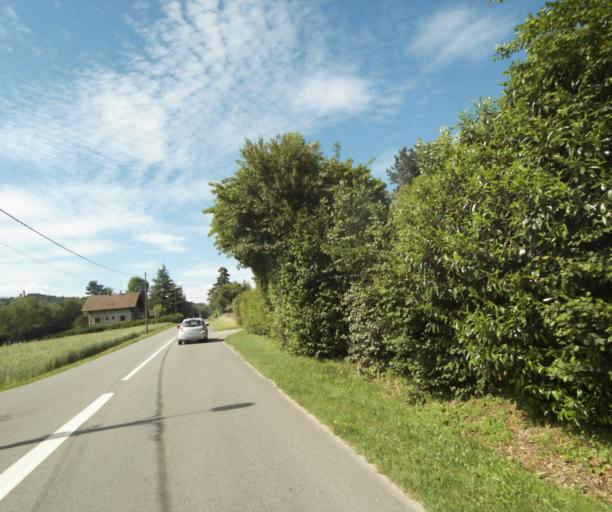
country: FR
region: Rhone-Alpes
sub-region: Departement de la Haute-Savoie
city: Allinges
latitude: 46.3213
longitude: 6.4748
